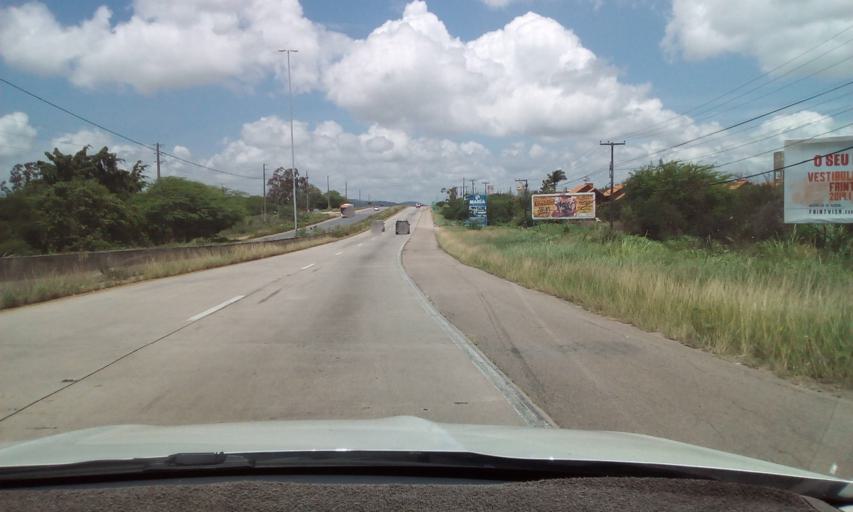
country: BR
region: Pernambuco
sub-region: Gravata
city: Gravata
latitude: -8.2044
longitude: -35.5998
